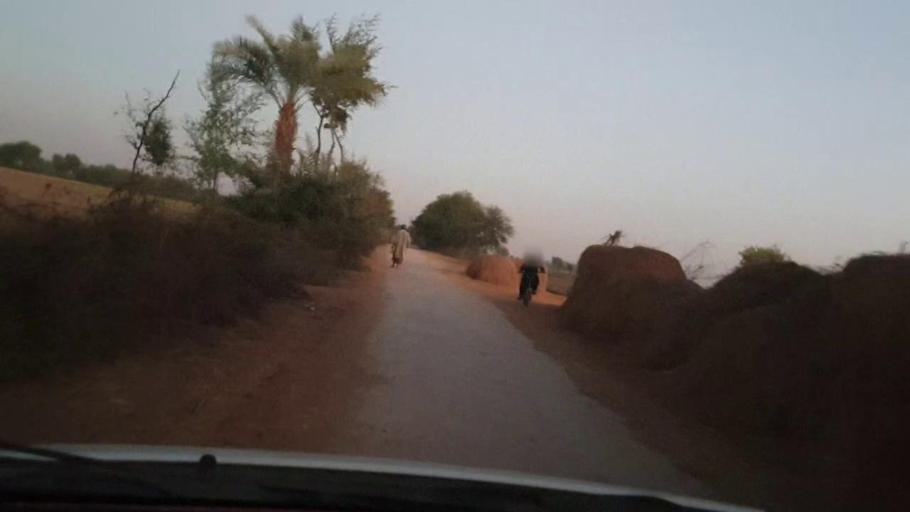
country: PK
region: Sindh
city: Khairpur Nathan Shah
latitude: 27.1334
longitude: 67.7231
